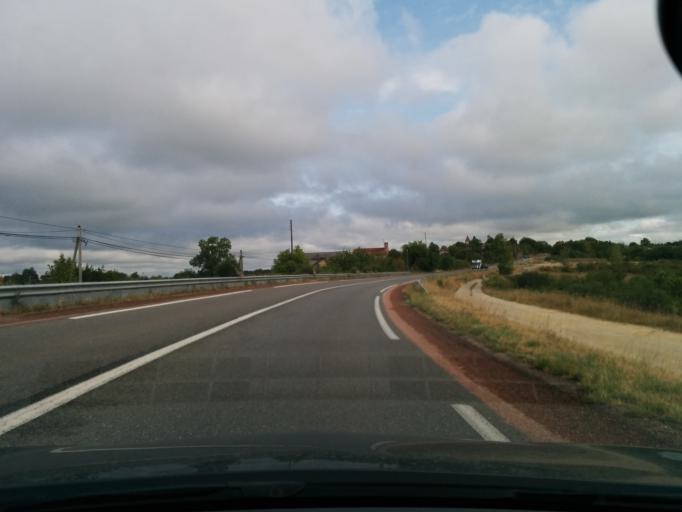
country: FR
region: Midi-Pyrenees
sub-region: Departement du Lot
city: Pradines
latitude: 44.4921
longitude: 1.4373
